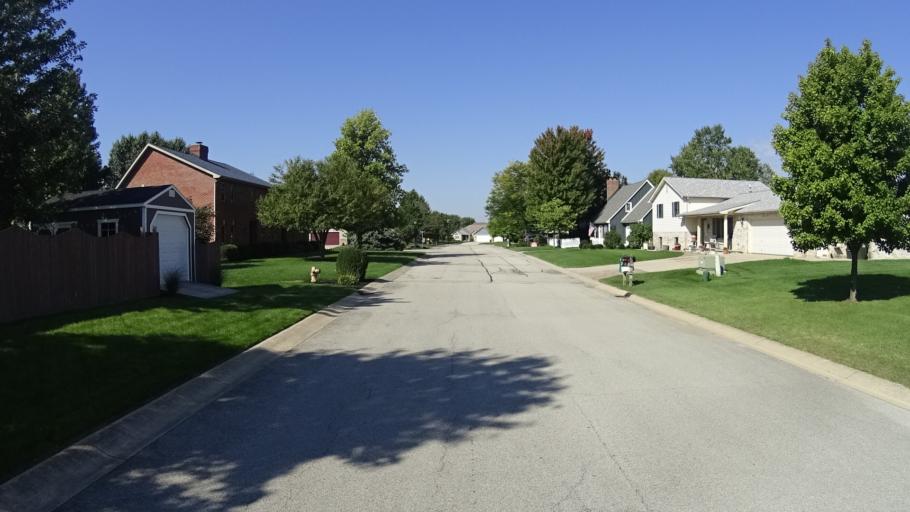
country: US
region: Indiana
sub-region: Madison County
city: Lapel
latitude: 40.0596
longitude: -85.8471
